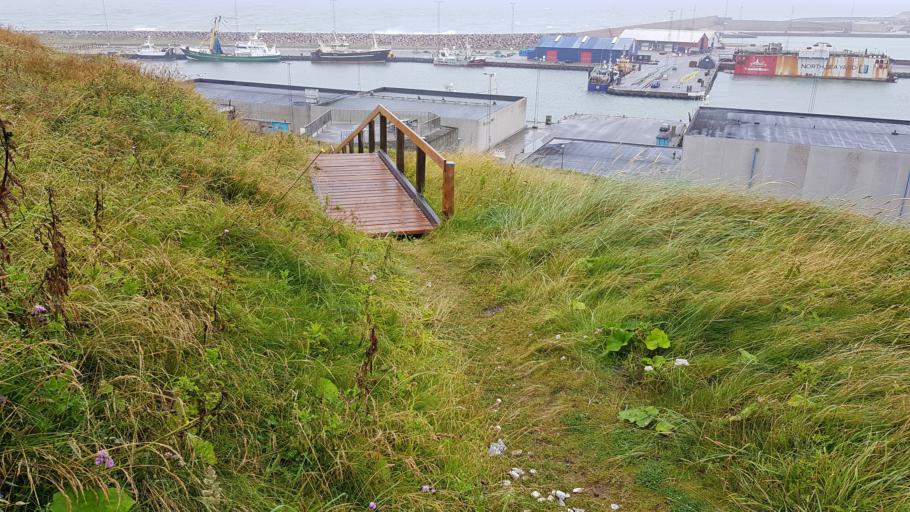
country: DK
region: North Denmark
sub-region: Thisted Kommune
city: Hanstholm
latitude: 57.1171
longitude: 8.5957
